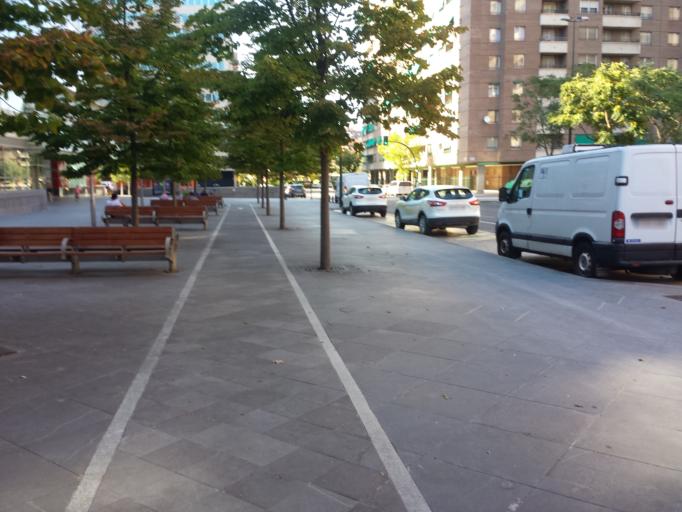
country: ES
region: Aragon
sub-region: Provincia de Zaragoza
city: Delicias
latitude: 41.6404
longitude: -0.9089
